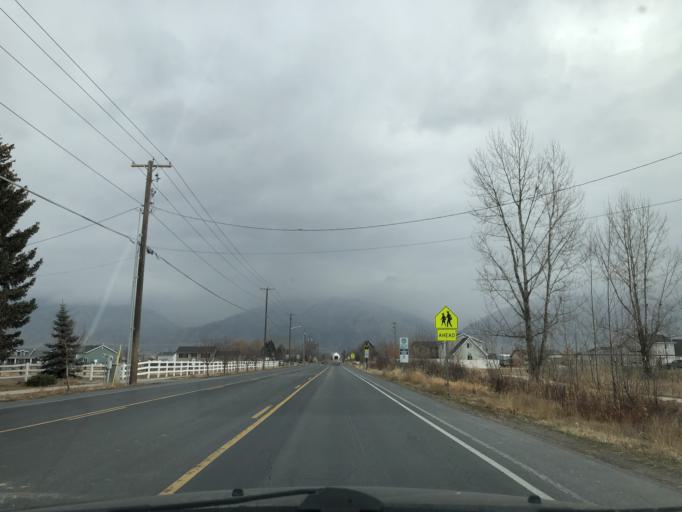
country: US
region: Utah
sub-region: Cache County
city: Nibley
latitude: 41.6751
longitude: -111.8667
